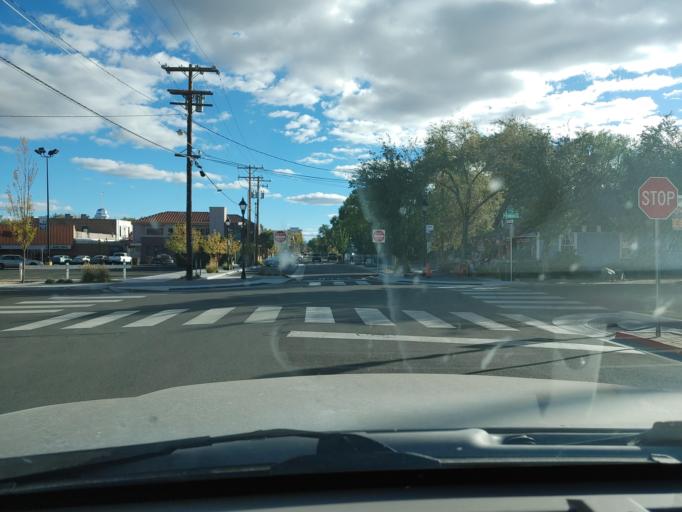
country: US
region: Nevada
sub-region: Carson City
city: Carson City
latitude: 39.1674
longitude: -119.7678
